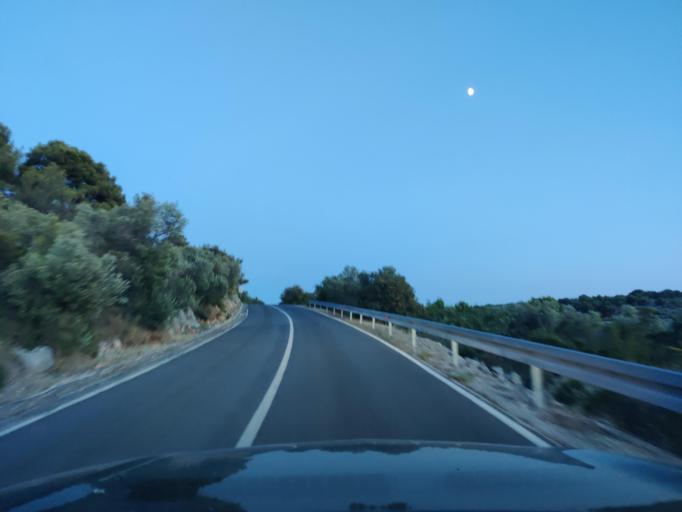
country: HR
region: Sibensko-Kniniska
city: Murter
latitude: 43.8160
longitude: 15.6002
